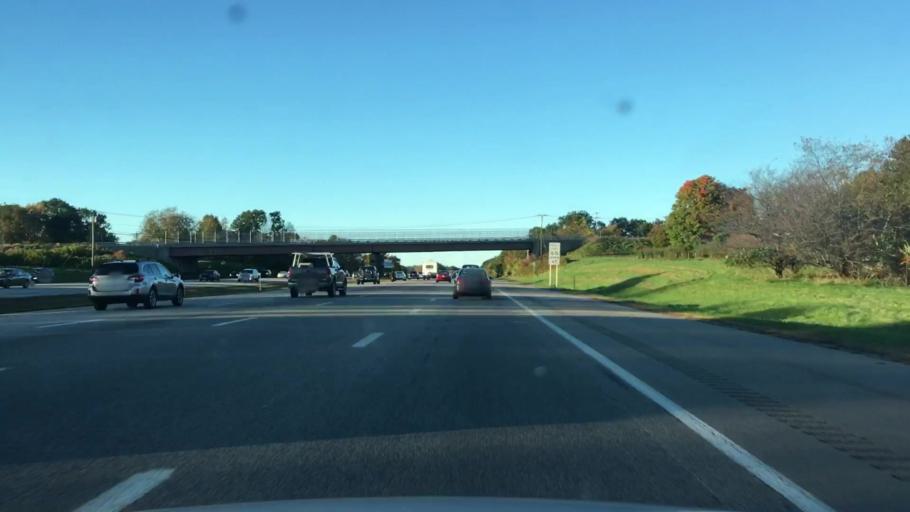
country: US
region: New Hampshire
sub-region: Rockingham County
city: North Hampton
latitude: 42.9728
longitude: -70.8540
